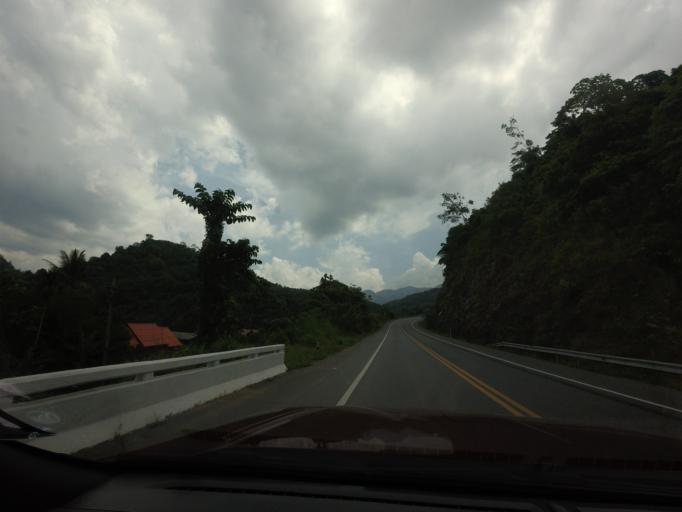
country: TH
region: Yala
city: Than To
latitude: 6.0516
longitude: 101.1967
